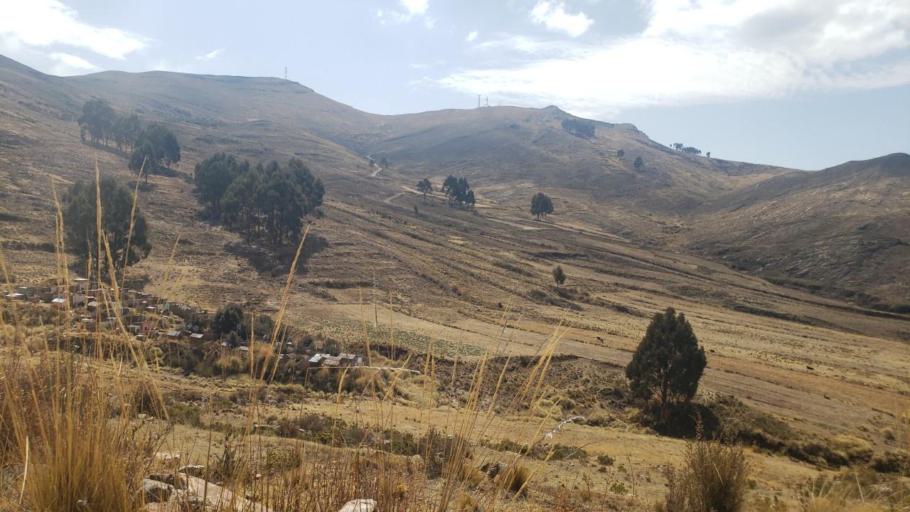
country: BO
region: La Paz
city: Batallas
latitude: -16.3482
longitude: -68.6458
